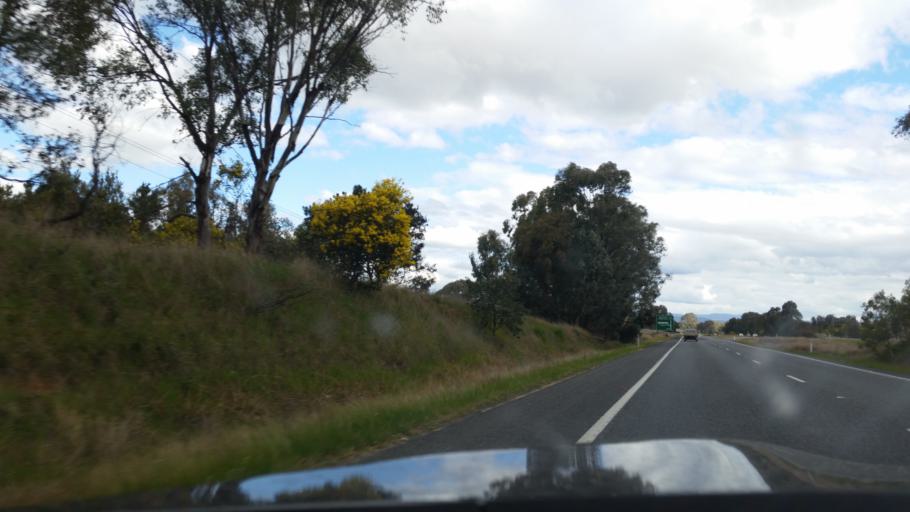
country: AU
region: New South Wales
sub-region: Albury Municipality
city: Lavington
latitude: -35.9882
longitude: 146.9968
